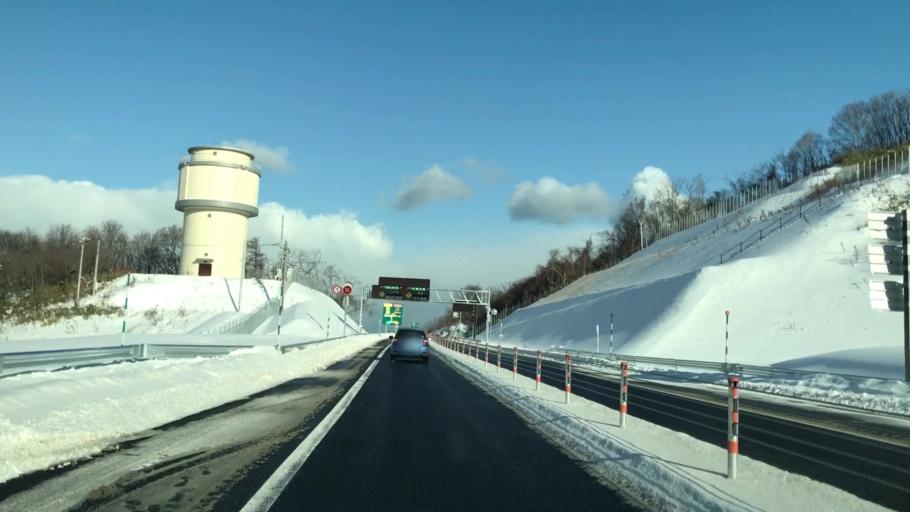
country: JP
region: Hokkaido
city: Otaru
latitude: 43.1586
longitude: 141.0516
